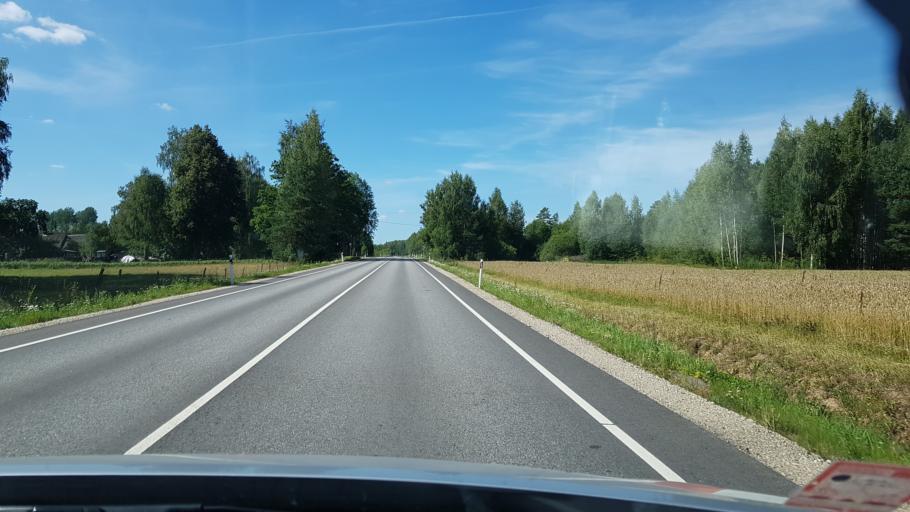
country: EE
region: Polvamaa
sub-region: Polva linn
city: Polva
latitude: 58.0044
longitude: 27.2087
